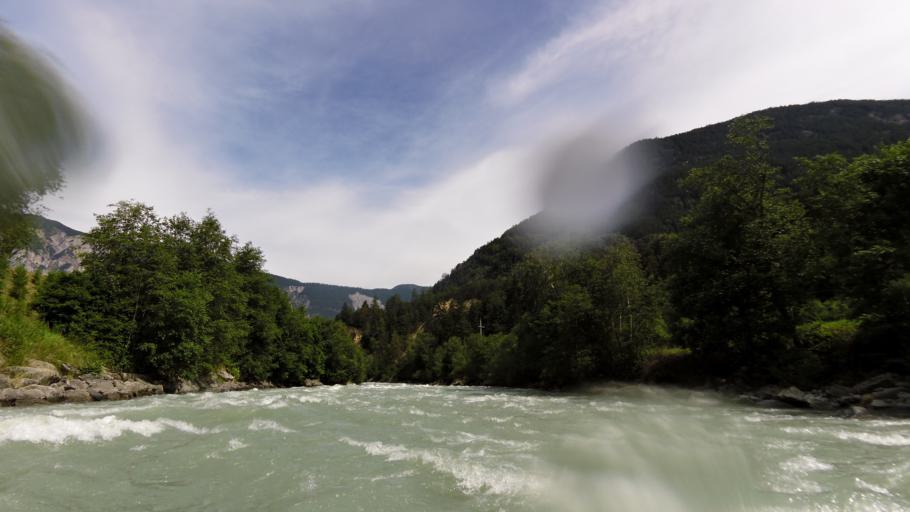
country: AT
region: Tyrol
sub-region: Politischer Bezirk Imst
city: Sautens
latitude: 47.2137
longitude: 10.8632
